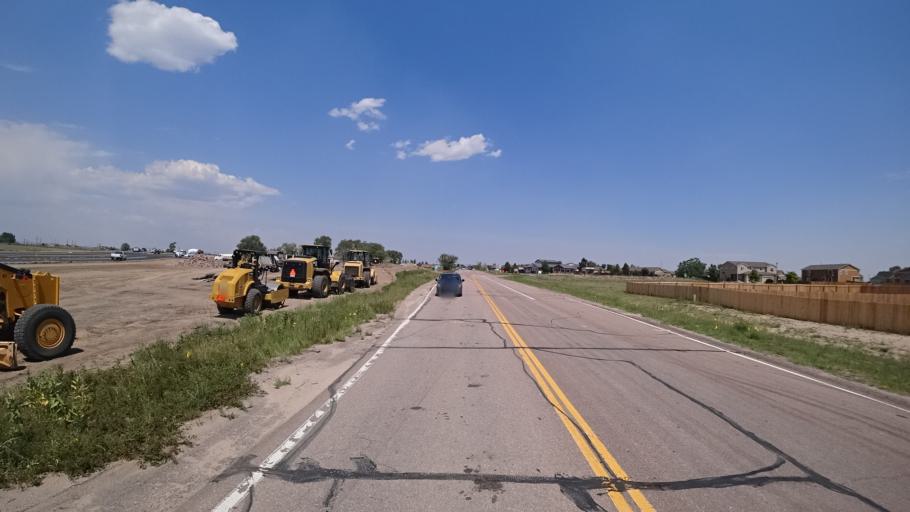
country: US
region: Colorado
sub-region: El Paso County
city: Cimarron Hills
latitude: 38.9290
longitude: -104.6081
